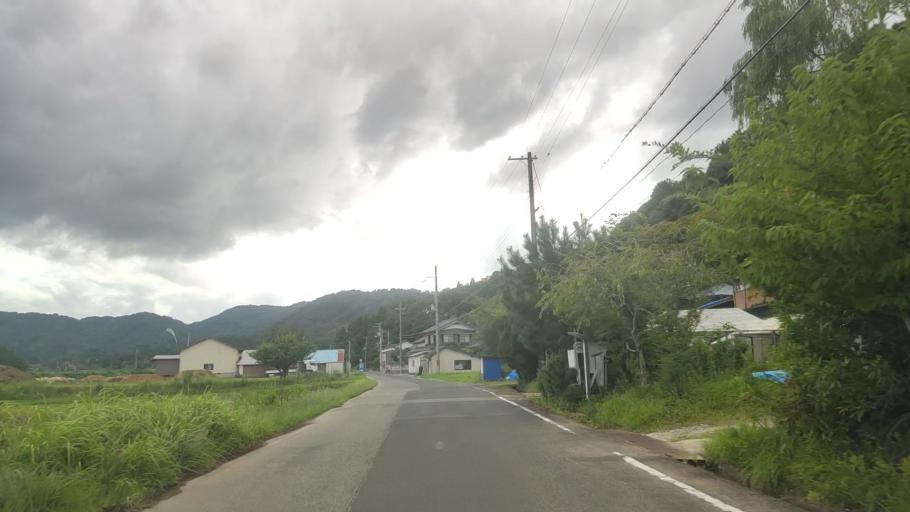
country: JP
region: Hyogo
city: Toyooka
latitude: 35.6024
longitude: 134.8898
